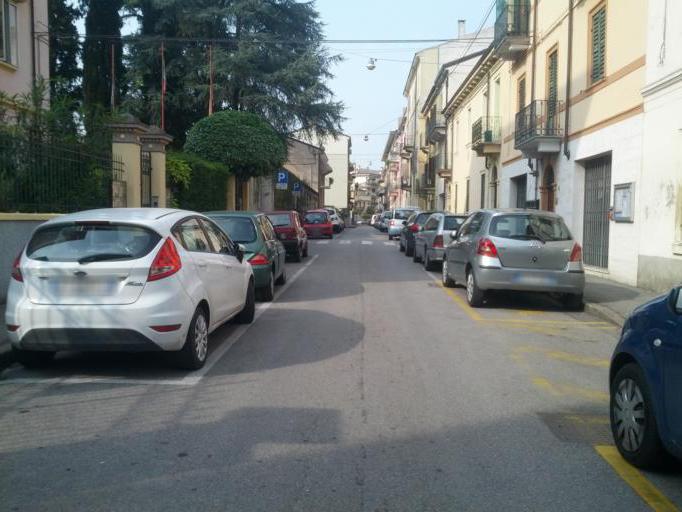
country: IT
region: Veneto
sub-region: Provincia di Verona
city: Poiano
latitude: 45.4408
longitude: 11.0177
